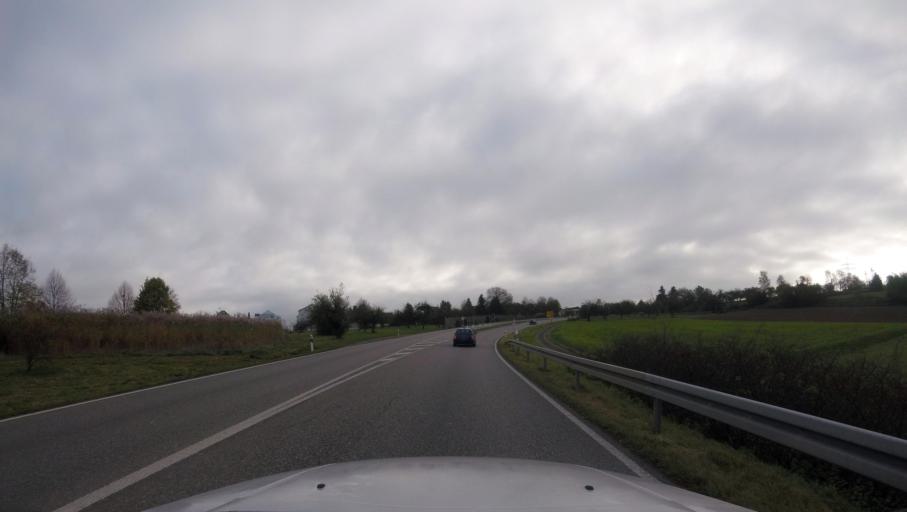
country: DE
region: Baden-Wuerttemberg
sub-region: Regierungsbezirk Stuttgart
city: Backnang
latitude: 48.9361
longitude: 9.4337
